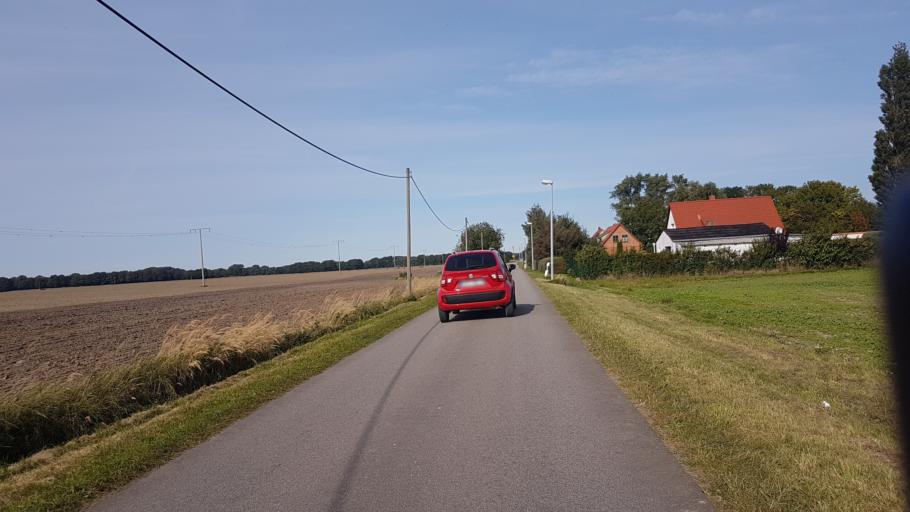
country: DE
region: Mecklenburg-Vorpommern
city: Gingst
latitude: 54.4258
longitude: 13.2238
